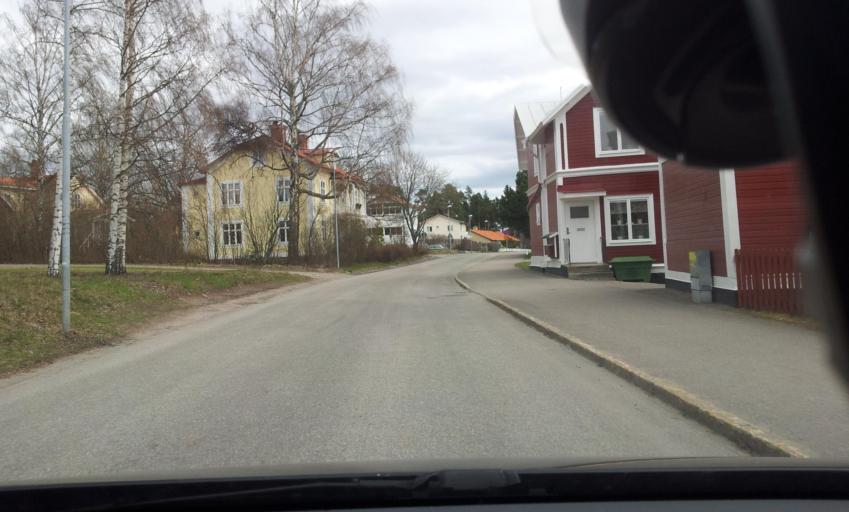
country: SE
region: Gaevleborg
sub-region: Ljusdals Kommun
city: Ljusdal
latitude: 61.8309
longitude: 16.0968
